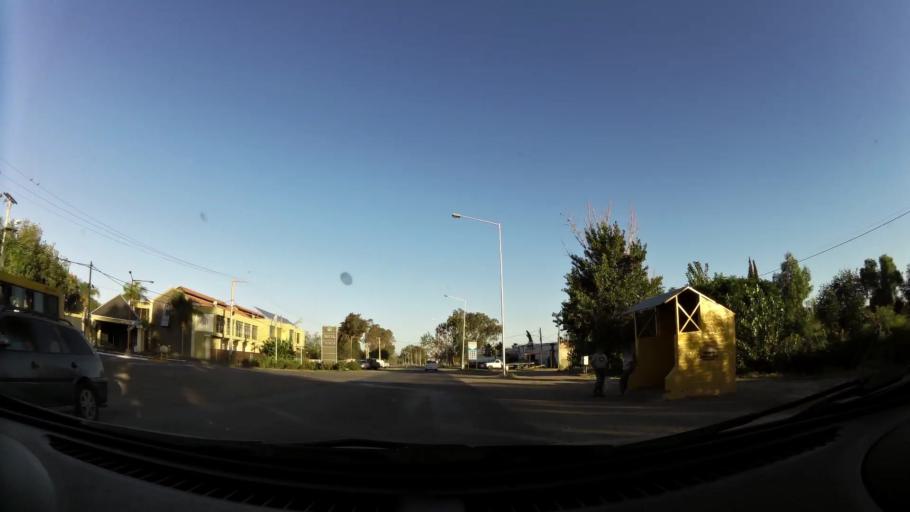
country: AR
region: San Juan
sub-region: Departamento de Santa Lucia
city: Santa Lucia
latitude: -31.5449
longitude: -68.4904
